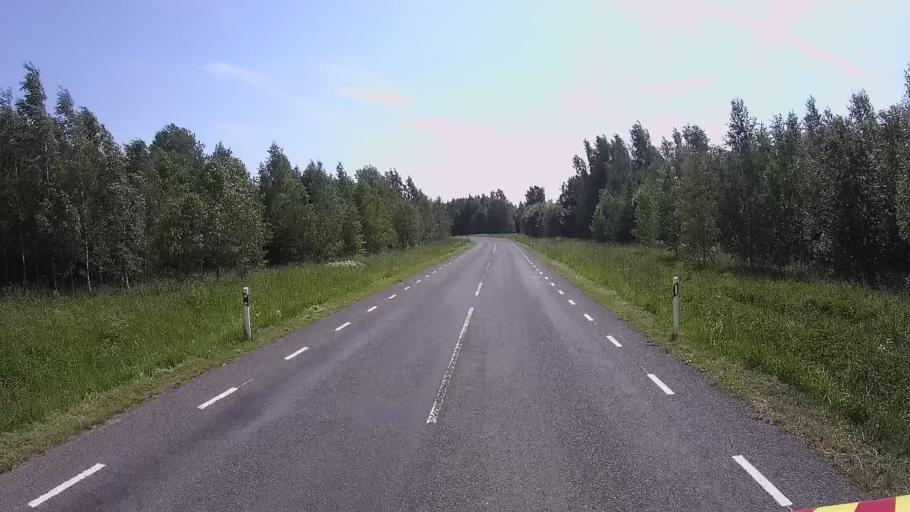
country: EE
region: Viljandimaa
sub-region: Karksi vald
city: Karksi-Nuia
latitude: 58.0462
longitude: 25.5457
